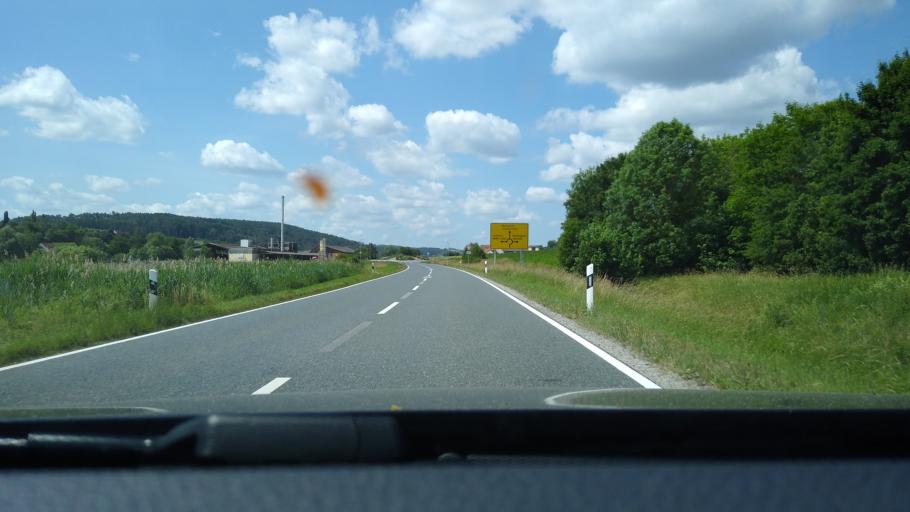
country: DE
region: Bavaria
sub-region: Regierungsbezirk Mittelfranken
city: Neuhof an der Zenn
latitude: 49.4616
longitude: 10.6444
